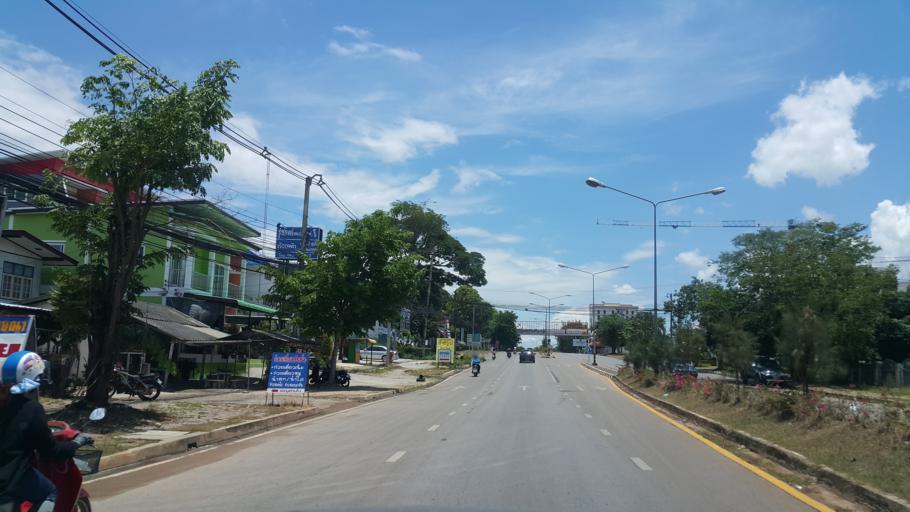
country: TH
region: Phayao
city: Phayao
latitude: 19.1930
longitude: 99.8778
